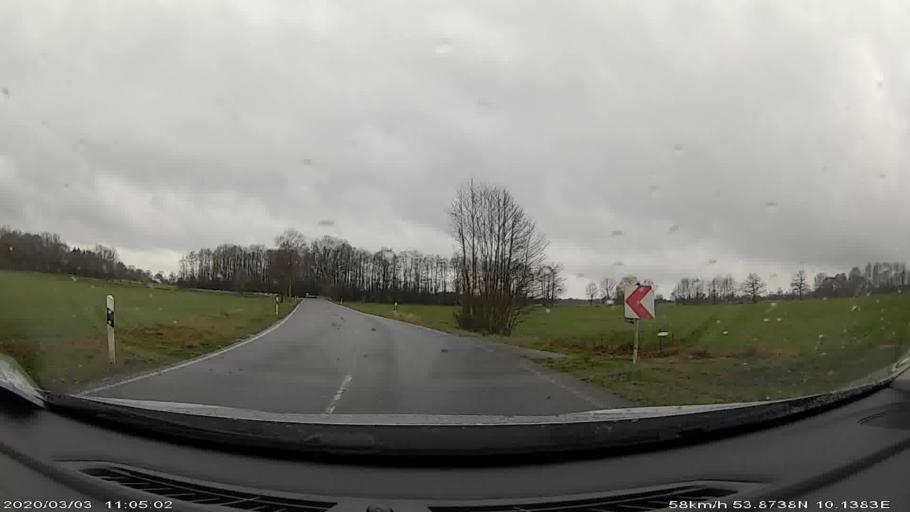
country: DE
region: Schleswig-Holstein
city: Stuvenborn
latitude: 53.8720
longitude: 10.1368
